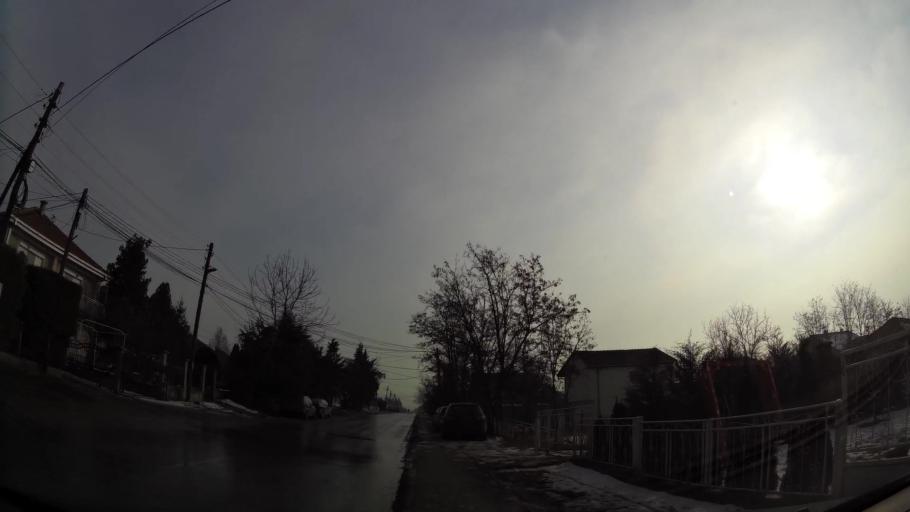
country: MK
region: Ilinden
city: Marino
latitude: 41.9922
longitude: 21.5895
